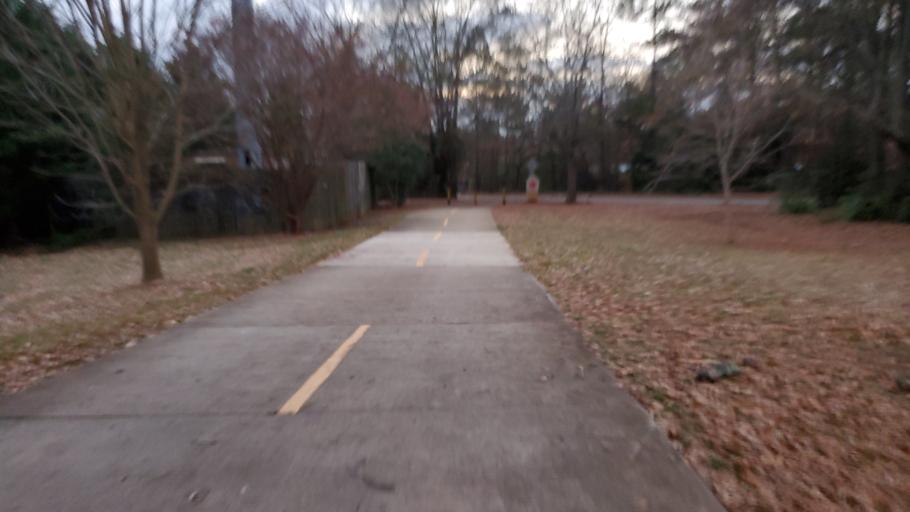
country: US
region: Georgia
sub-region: DeKalb County
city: Avondale Estates
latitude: 33.7798
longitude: -84.2668
